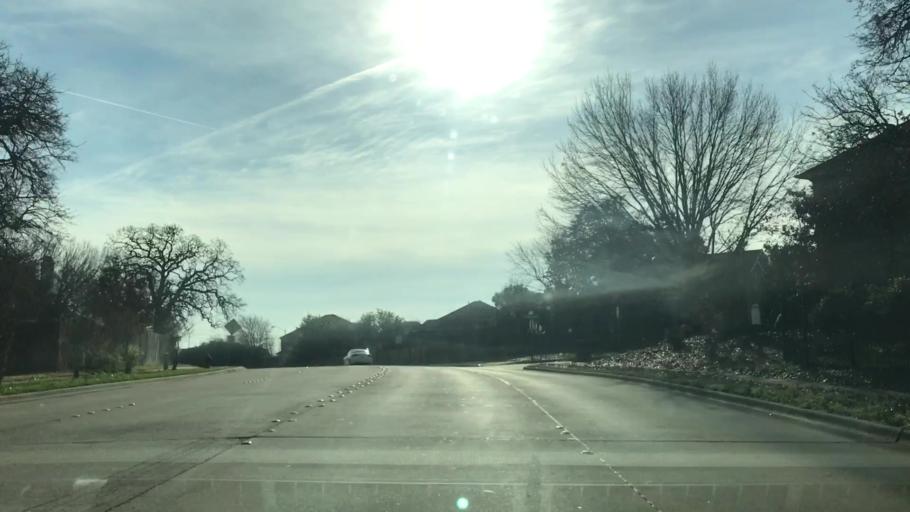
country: US
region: Texas
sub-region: Tarrant County
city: Colleyville
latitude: 32.8922
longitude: -97.2064
